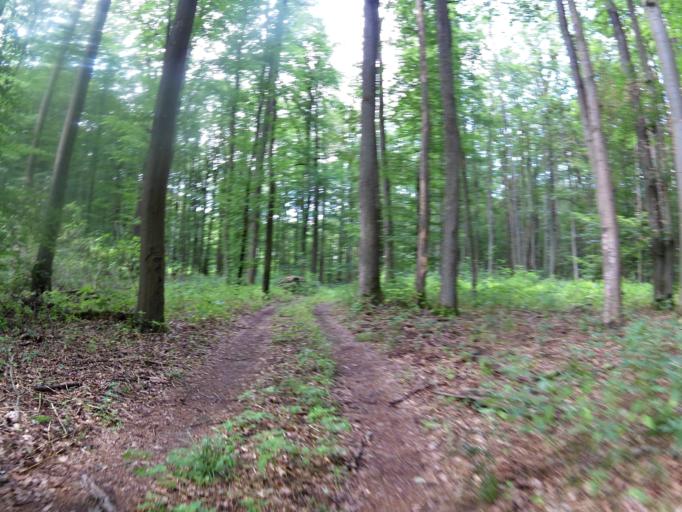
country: DE
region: Bavaria
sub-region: Regierungsbezirk Unterfranken
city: Kleinrinderfeld
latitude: 49.7023
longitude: 9.8763
